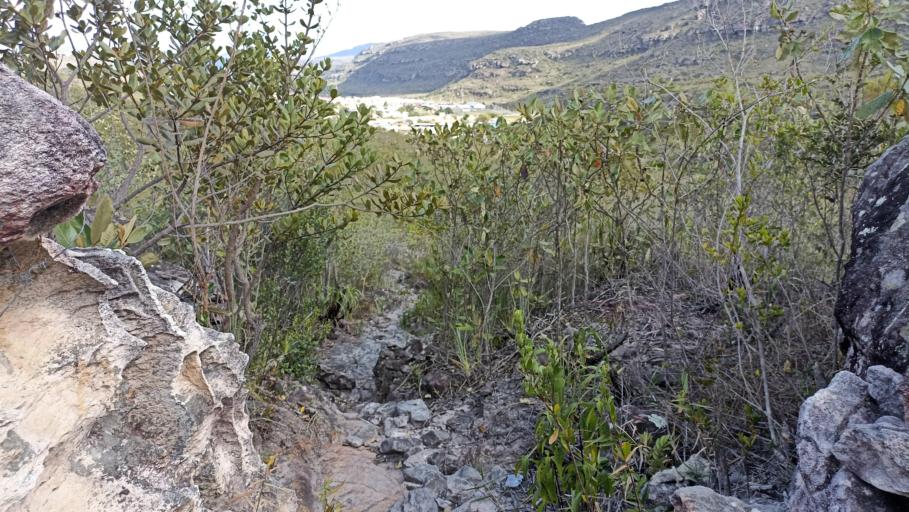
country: BR
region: Bahia
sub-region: Andarai
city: Vera Cruz
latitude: -12.9975
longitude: -41.3765
